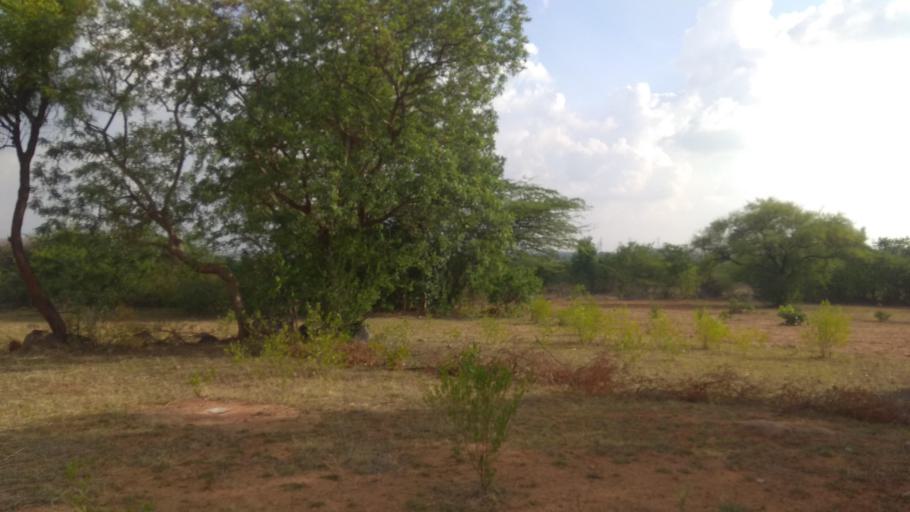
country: IN
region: Telangana
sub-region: Mahbubnagar
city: Farrukhnagar
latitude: 16.8880
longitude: 78.4785
